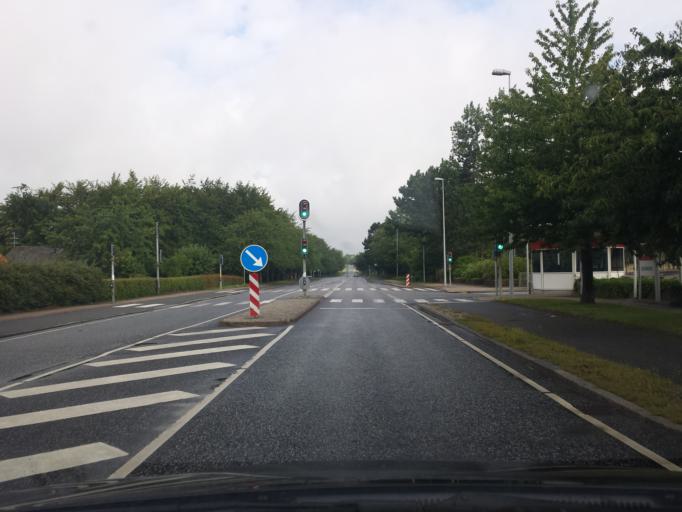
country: DK
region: South Denmark
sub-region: Sonderborg Kommune
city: Guderup
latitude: 55.0350
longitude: 9.8135
